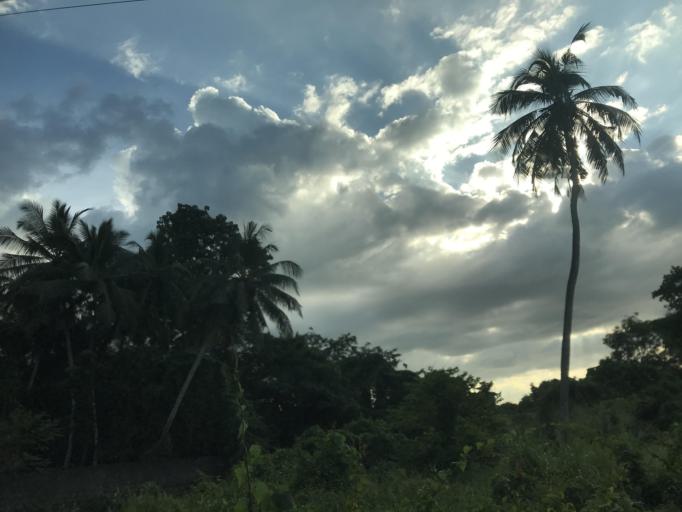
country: LK
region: Western
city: Gampaha
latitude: 7.1009
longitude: 79.9806
